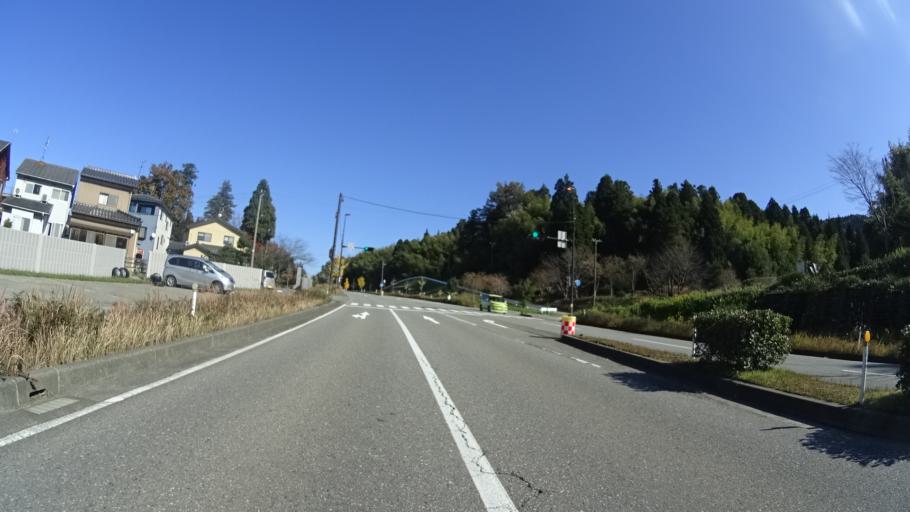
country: JP
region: Ishikawa
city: Nonoichi
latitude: 36.5027
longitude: 136.6238
